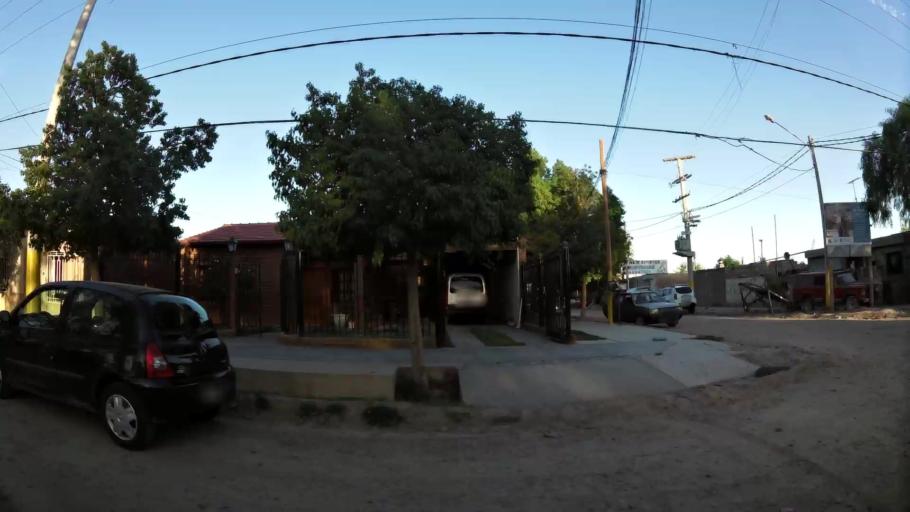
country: AR
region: San Juan
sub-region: Departamento de Santa Lucia
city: Santa Lucia
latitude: -31.5395
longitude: -68.4937
